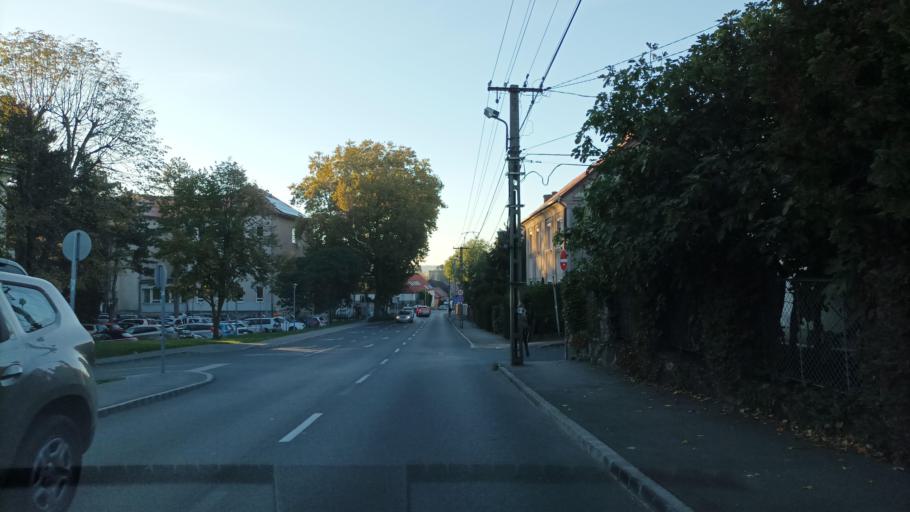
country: HU
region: Baranya
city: Pecs
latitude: 46.0733
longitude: 18.2041
